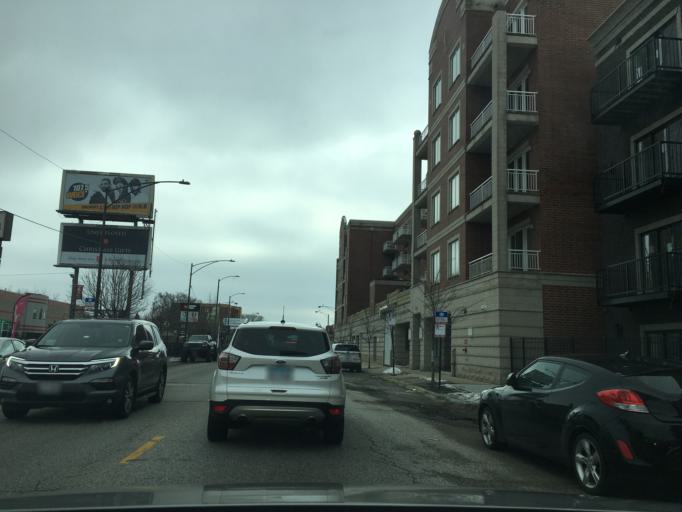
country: US
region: Illinois
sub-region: Cook County
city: Harwood Heights
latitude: 41.9466
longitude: -87.8071
